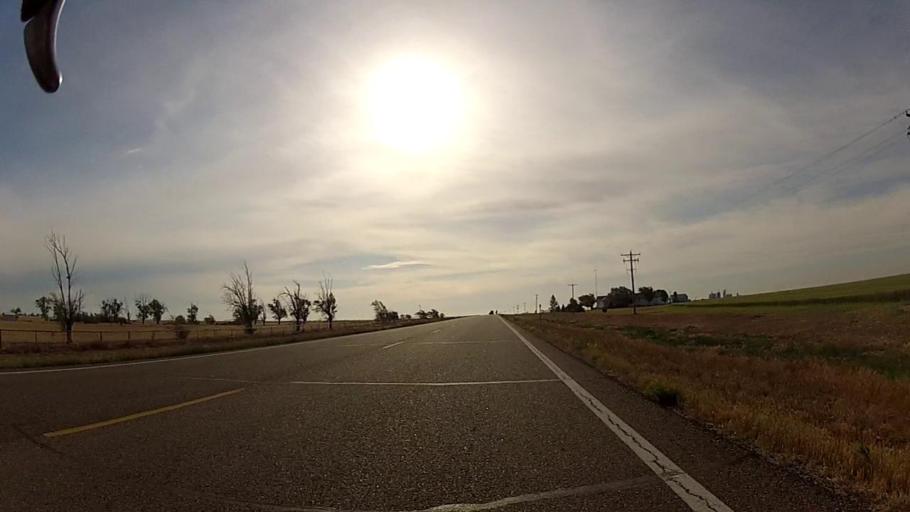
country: US
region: Kansas
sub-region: Grant County
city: Ulysses
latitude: 37.5766
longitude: -101.4851
